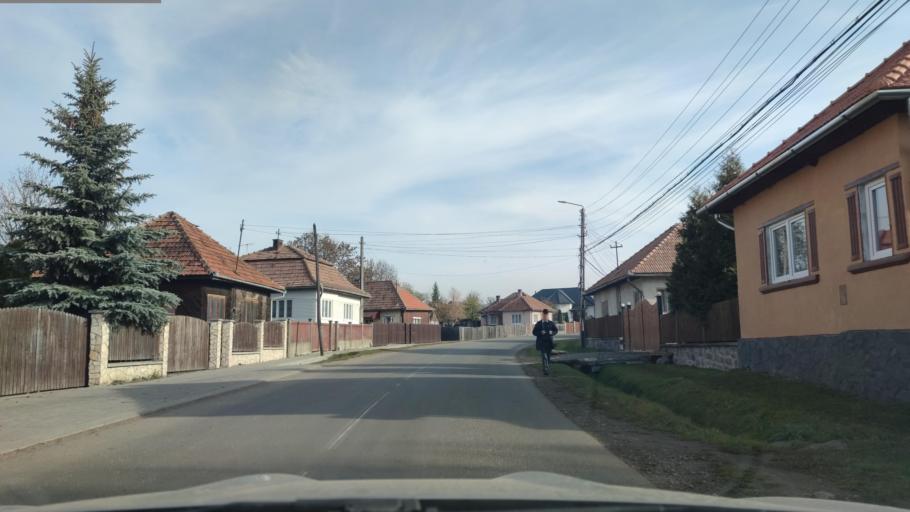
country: RO
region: Harghita
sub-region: Comuna Ditrau
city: Ditrau
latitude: 46.8085
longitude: 25.5075
